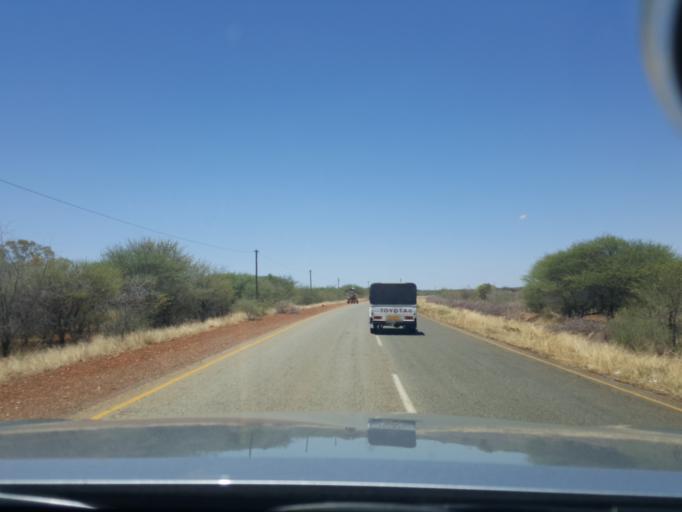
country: BW
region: South East
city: Otse
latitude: -25.1030
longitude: 25.9612
